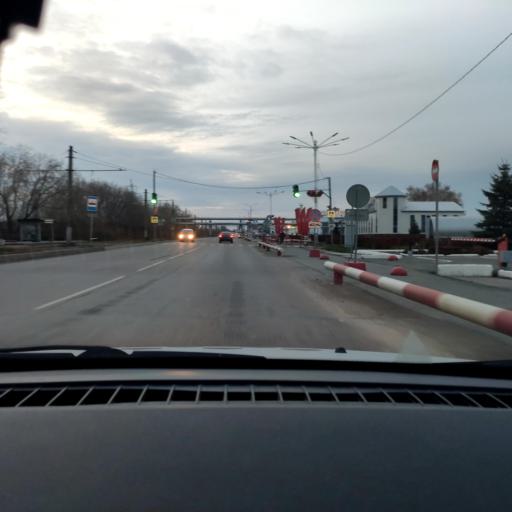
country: RU
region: Perm
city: Kondratovo
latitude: 57.9238
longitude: 56.1395
